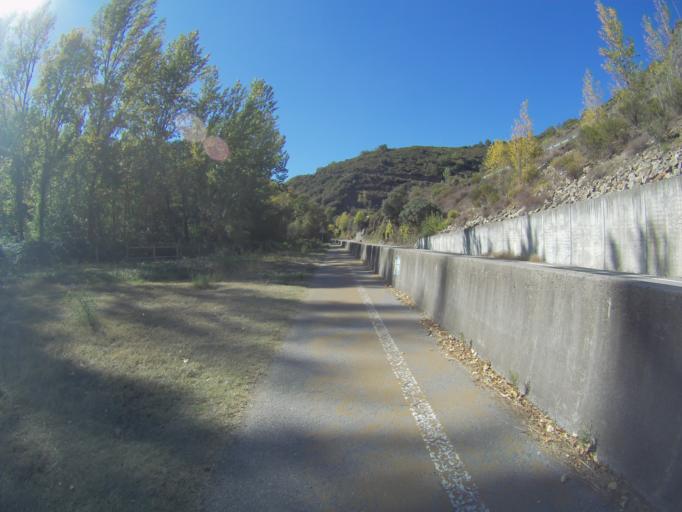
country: ES
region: Castille and Leon
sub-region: Provincia de Leon
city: Trabadelo
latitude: 42.6386
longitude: -6.8580
